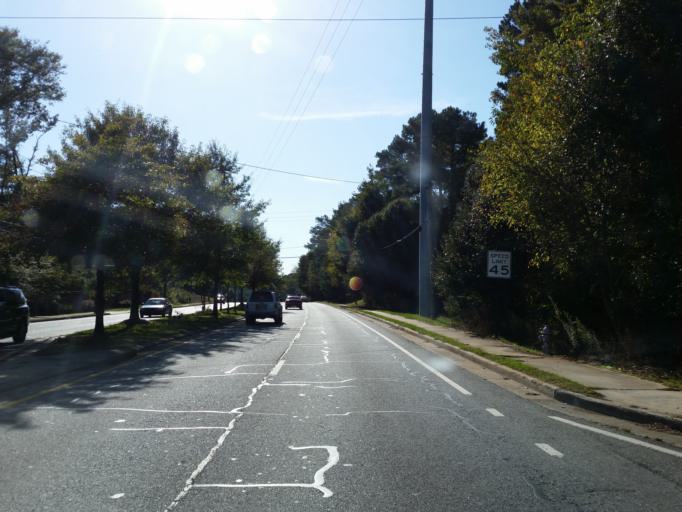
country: US
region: Georgia
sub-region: Cherokee County
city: Woodstock
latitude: 34.0248
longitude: -84.4825
